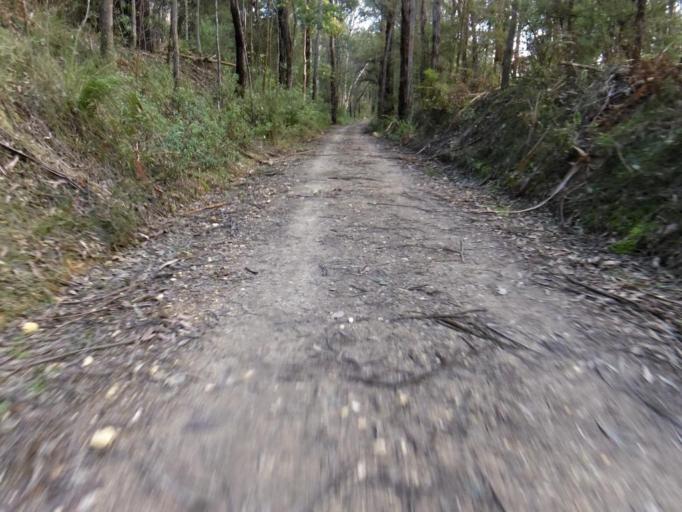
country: AU
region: Victoria
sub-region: Baw Baw
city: Warragul
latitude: -38.0608
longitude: 145.9475
